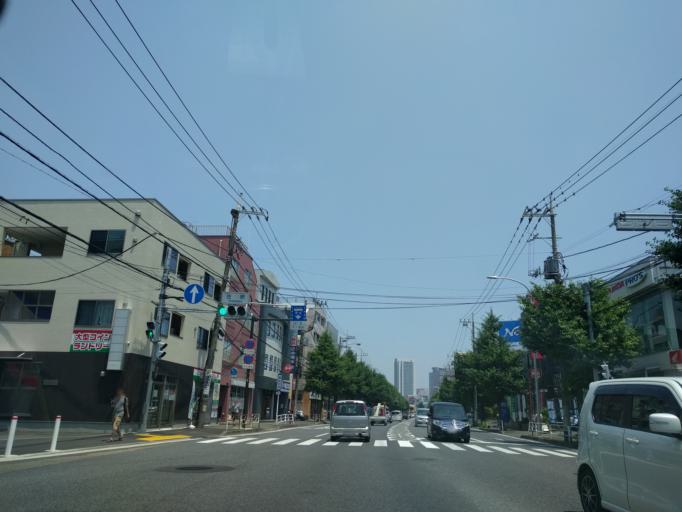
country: JP
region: Kanagawa
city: Yokohama
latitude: 35.3978
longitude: 139.5873
